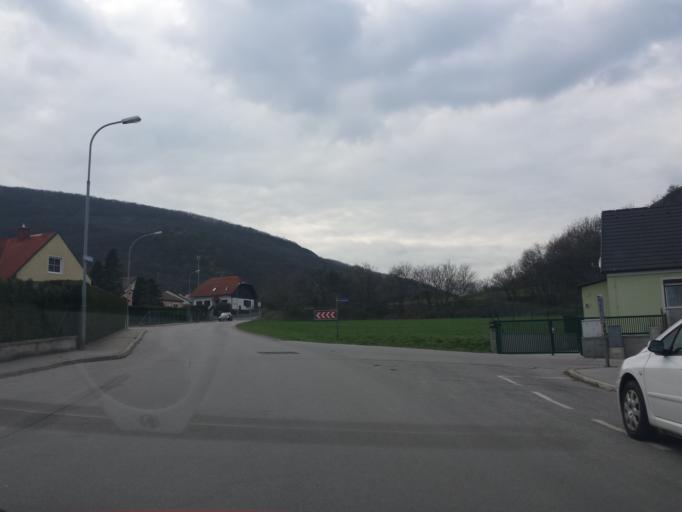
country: AT
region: Lower Austria
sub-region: Politischer Bezirk Bruck an der Leitha
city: Hainburg an der Donau
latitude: 48.1404
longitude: 16.9507
